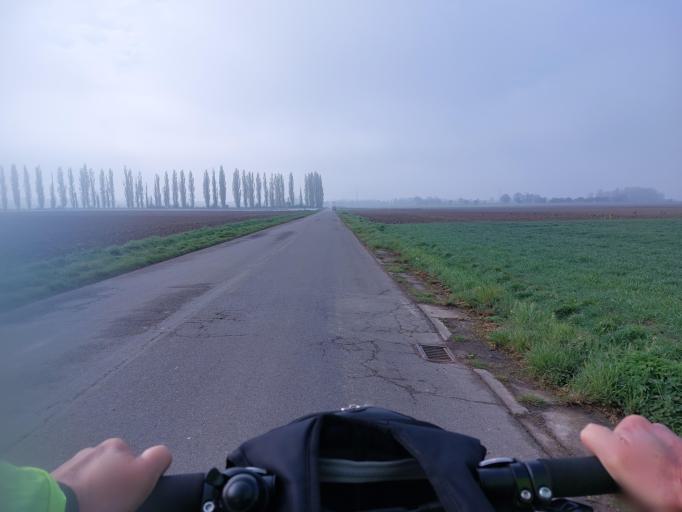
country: BE
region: Wallonia
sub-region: Province du Hainaut
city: Estinnes-au-Val
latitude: 50.4449
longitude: 4.0504
